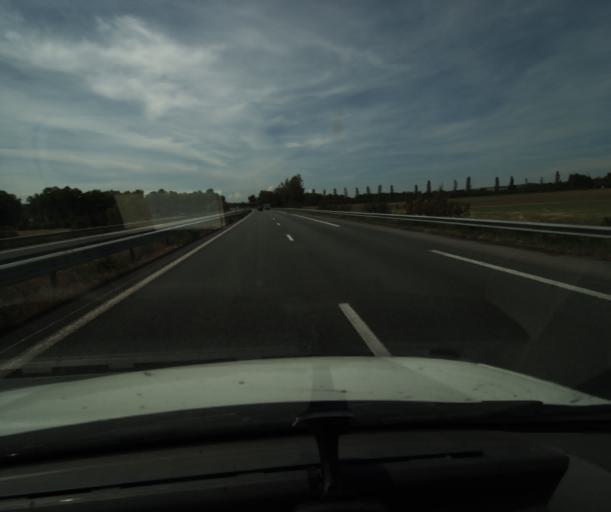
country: FR
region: Languedoc-Roussillon
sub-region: Departement de l'Aude
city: Castelnaudary
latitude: 43.2826
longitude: 1.9780
